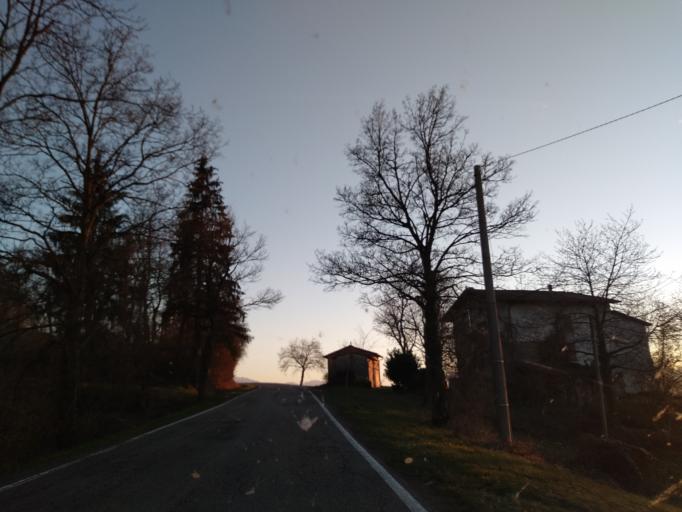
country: IT
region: Emilia-Romagna
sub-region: Provincia di Reggio Emilia
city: Castelnovo ne'Monti
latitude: 44.4251
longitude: 10.4059
